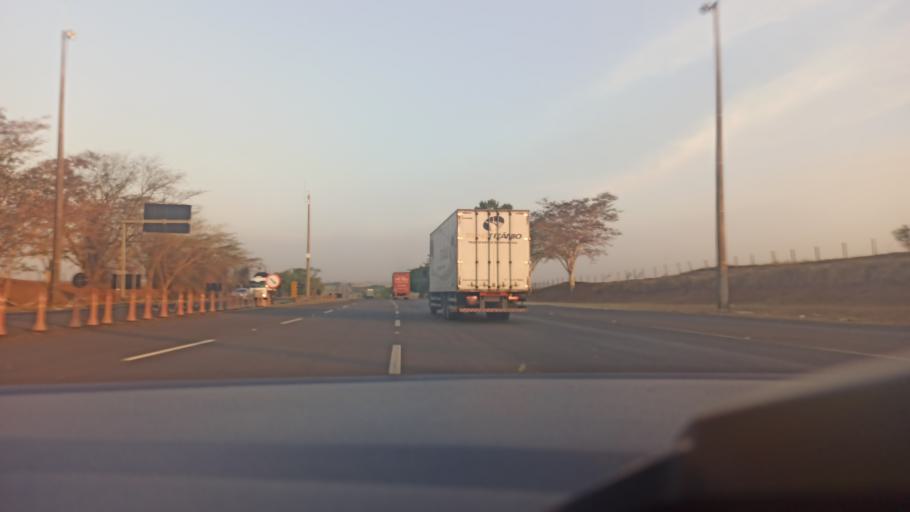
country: BR
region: Sao Paulo
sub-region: Santa Adelia
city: Santa Adelia
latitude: -21.3845
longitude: -48.7300
